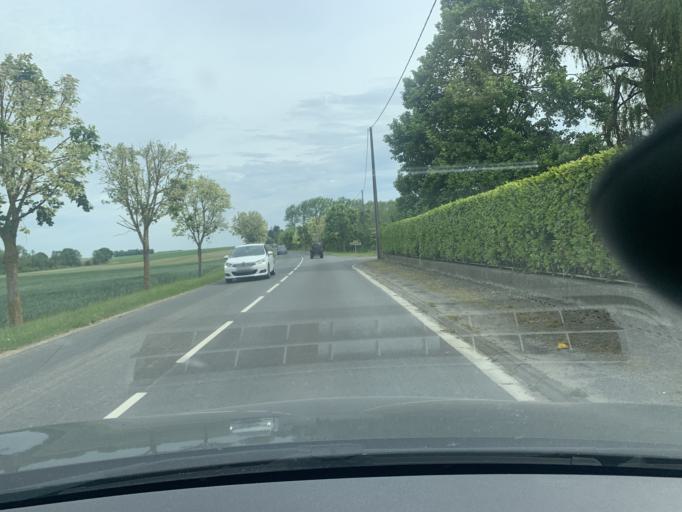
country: FR
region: Nord-Pas-de-Calais
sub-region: Departement du Nord
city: Marcoing
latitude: 50.1281
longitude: 3.1911
